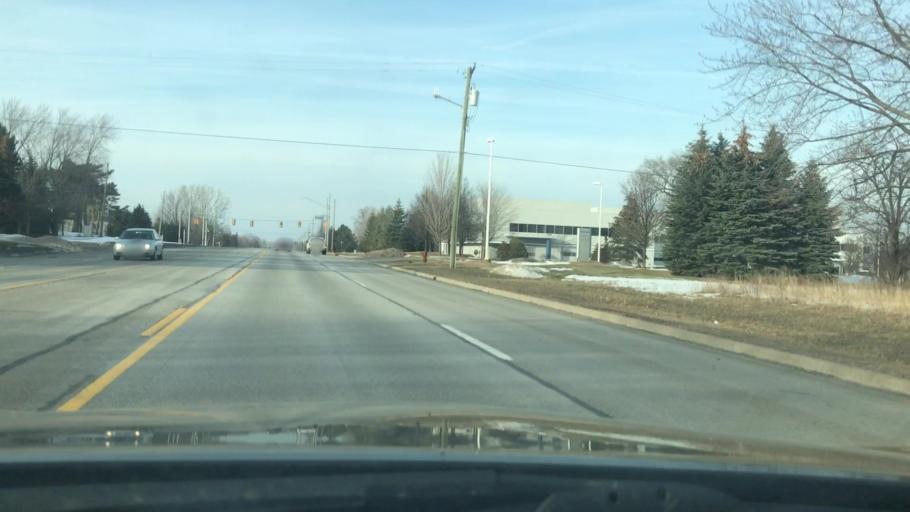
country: US
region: Michigan
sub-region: Oakland County
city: Novi
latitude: 42.4576
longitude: -83.4344
